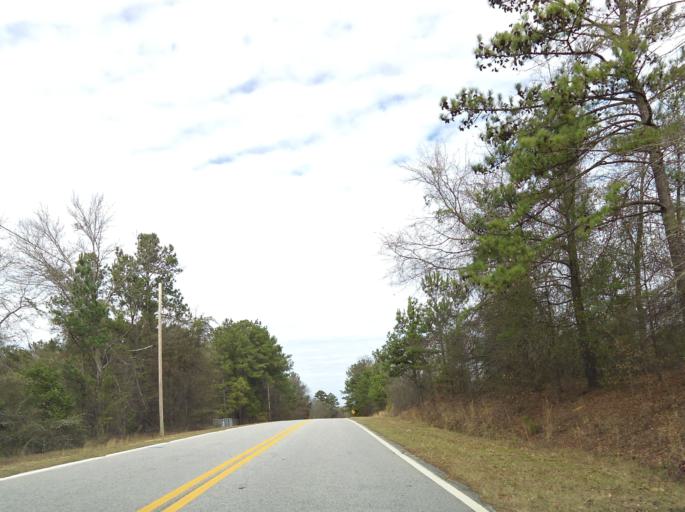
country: US
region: Georgia
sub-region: Bibb County
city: West Point
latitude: 32.8179
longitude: -83.7361
